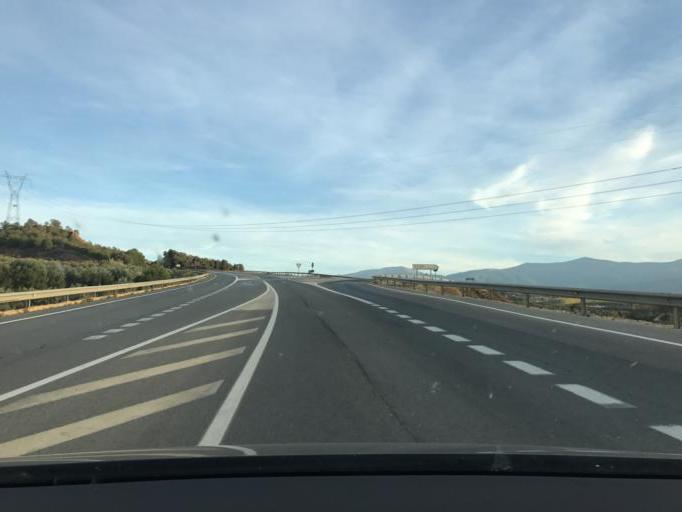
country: ES
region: Andalusia
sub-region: Provincia de Granada
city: Guadix
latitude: 37.2748
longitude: -3.1098
